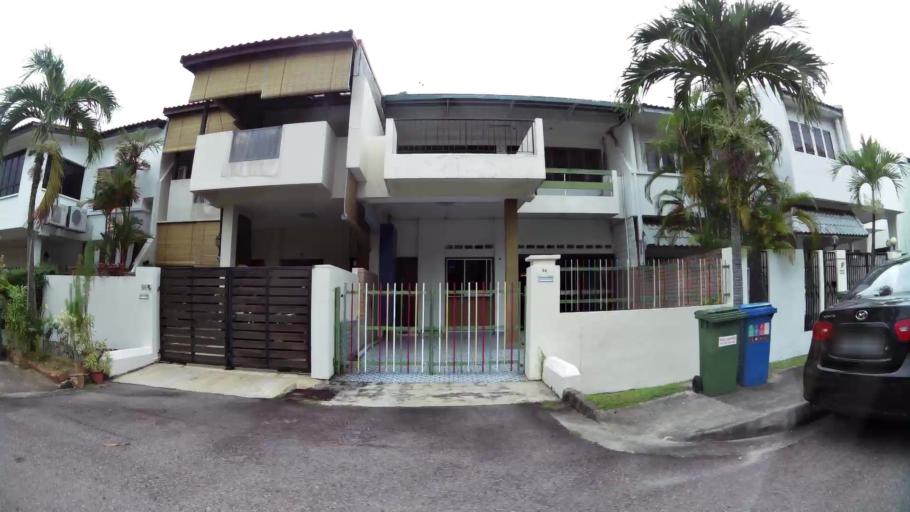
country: SG
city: Singapore
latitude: 1.3571
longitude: 103.8626
